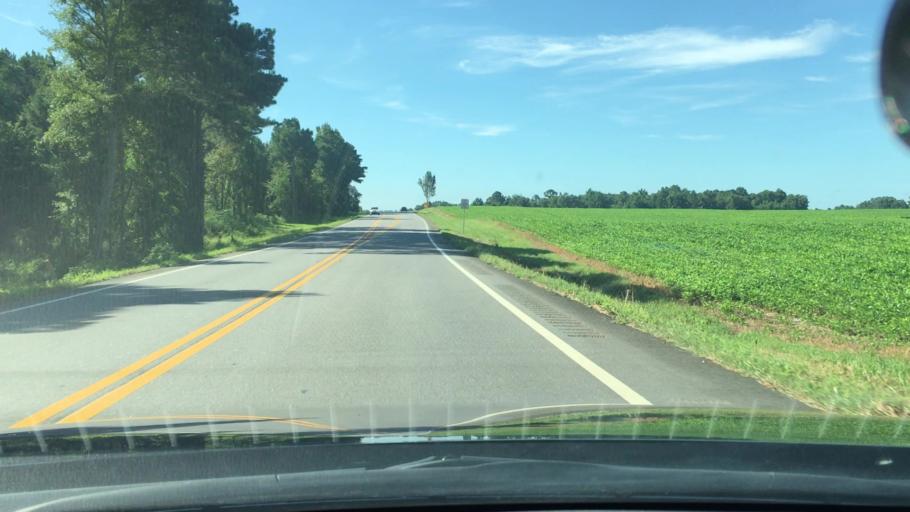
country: US
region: Georgia
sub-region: Putnam County
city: Jefferson
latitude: 33.4522
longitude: -83.4086
